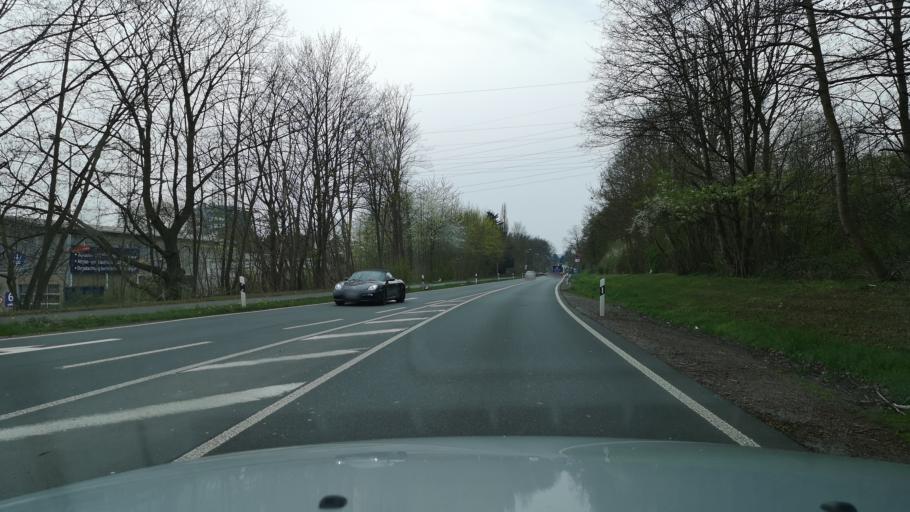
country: DE
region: North Rhine-Westphalia
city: Herdecke
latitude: 51.4034
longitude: 7.4725
